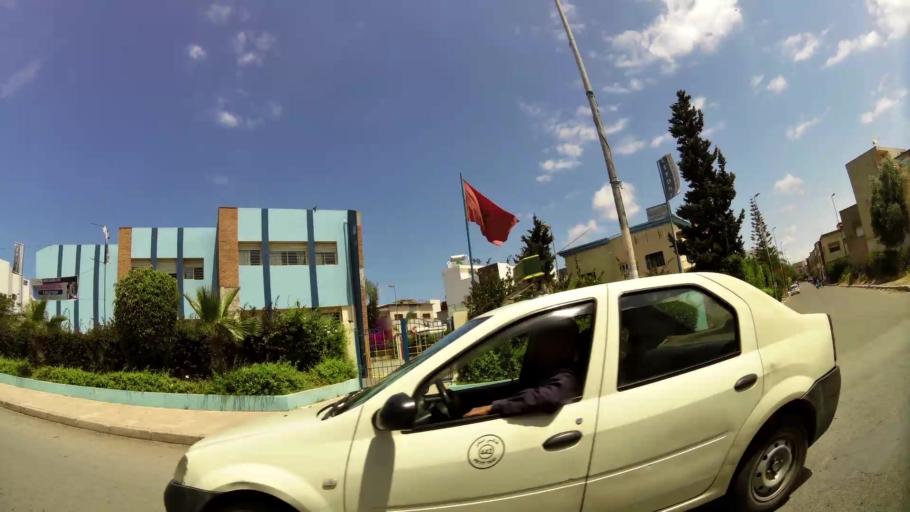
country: MA
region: Gharb-Chrarda-Beni Hssen
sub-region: Kenitra Province
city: Kenitra
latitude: 34.2659
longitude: -6.6116
